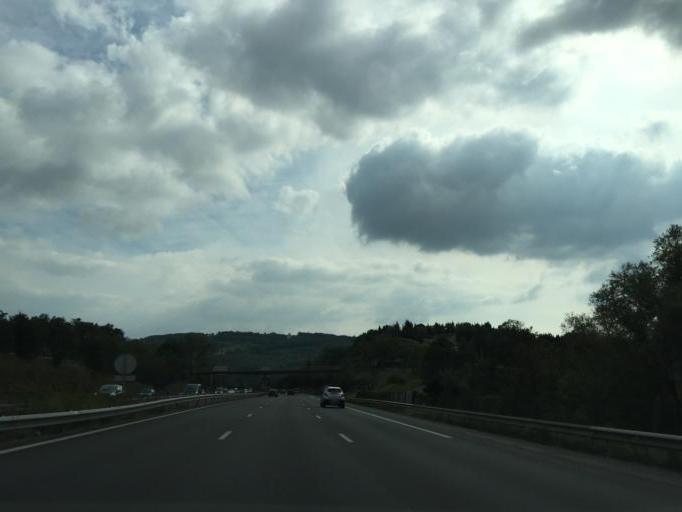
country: FR
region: Rhone-Alpes
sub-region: Departement de la Loire
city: La Fouillouse
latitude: 45.5121
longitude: 4.3013
